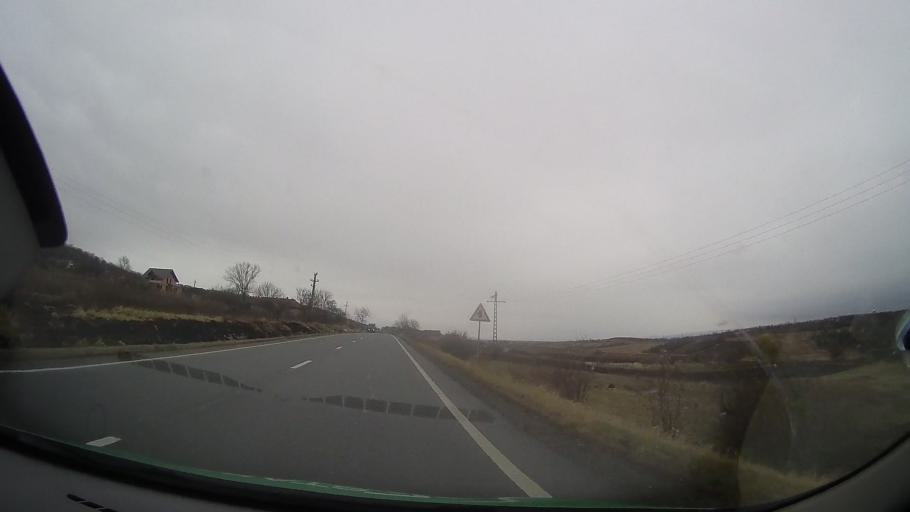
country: RO
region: Mures
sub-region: Comuna Breaza
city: Breaza
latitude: 46.7760
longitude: 24.6563
